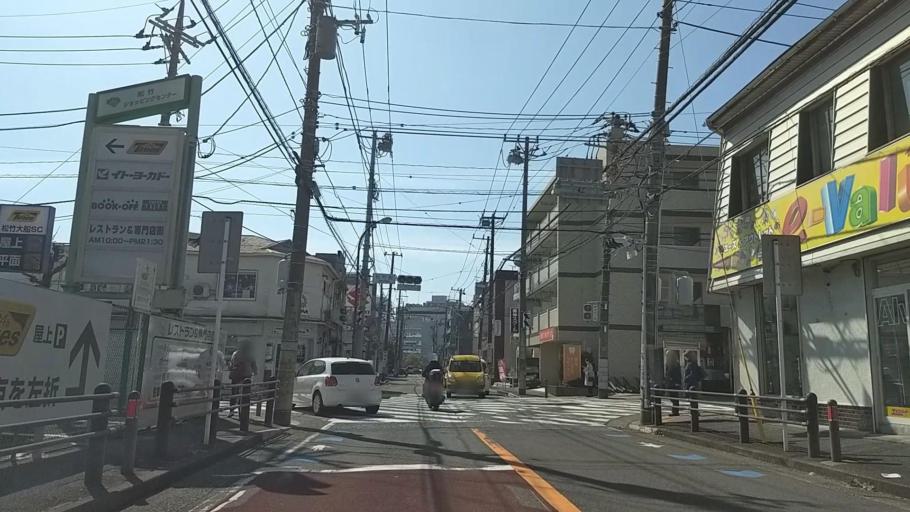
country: JP
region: Kanagawa
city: Kamakura
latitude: 35.3537
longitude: 139.5373
